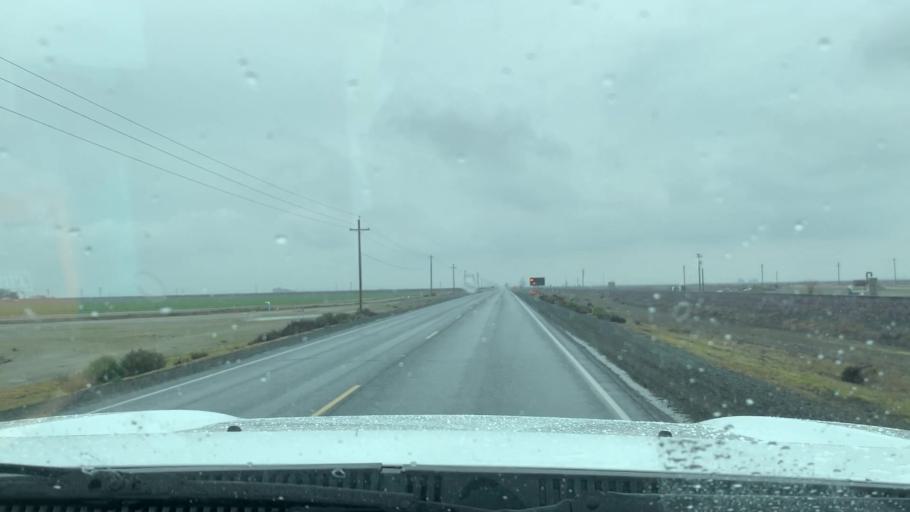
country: US
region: California
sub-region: Kings County
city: Corcoran
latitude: 36.0109
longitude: -119.4926
